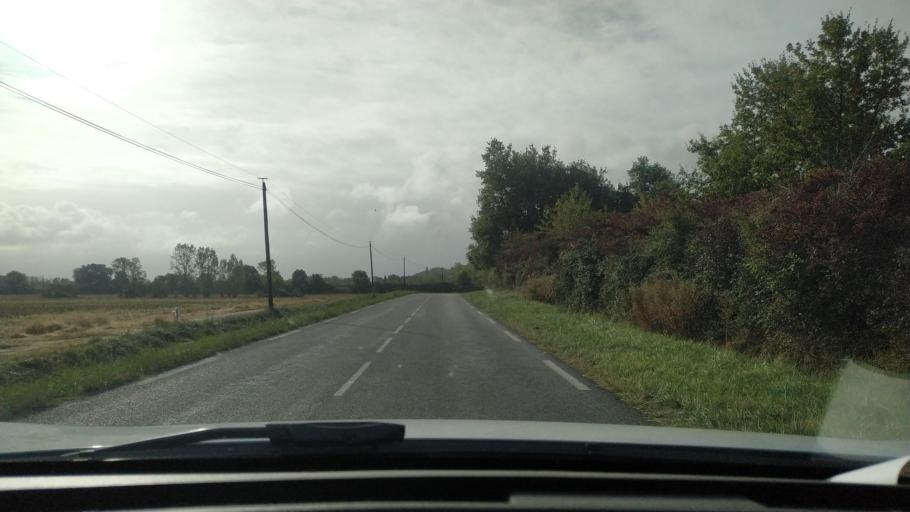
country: FR
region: Midi-Pyrenees
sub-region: Departement de la Haute-Garonne
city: Auterive
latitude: 43.3222
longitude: 1.4461
